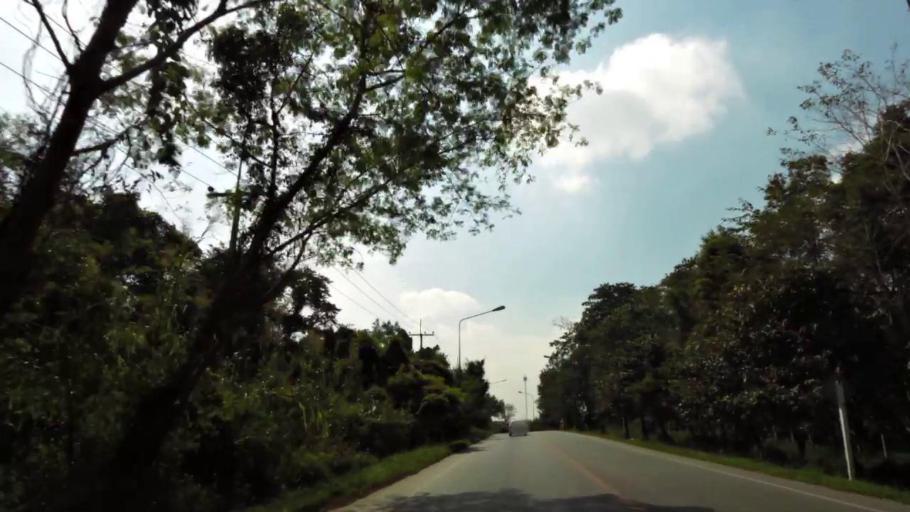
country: TH
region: Chiang Rai
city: Chiang Rai
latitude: 19.8708
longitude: 99.7797
